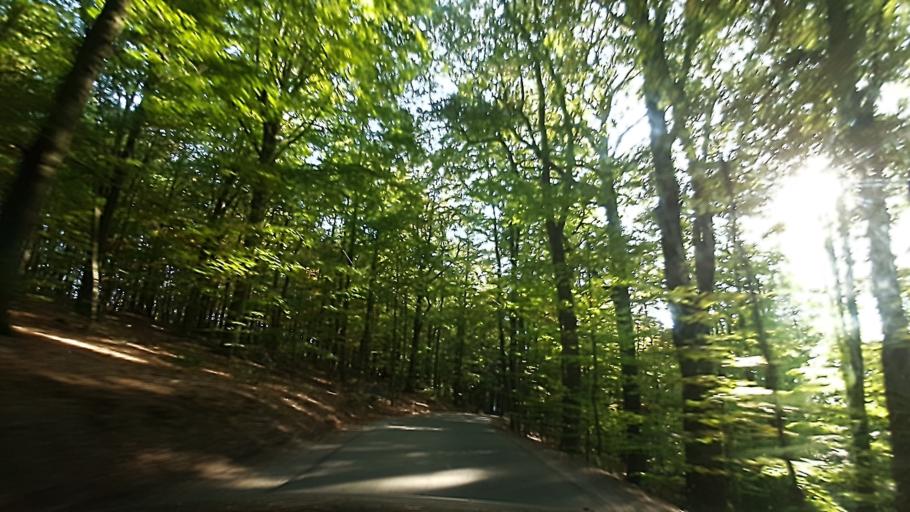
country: DE
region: North Rhine-Westphalia
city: Halver
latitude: 51.1334
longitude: 7.4836
